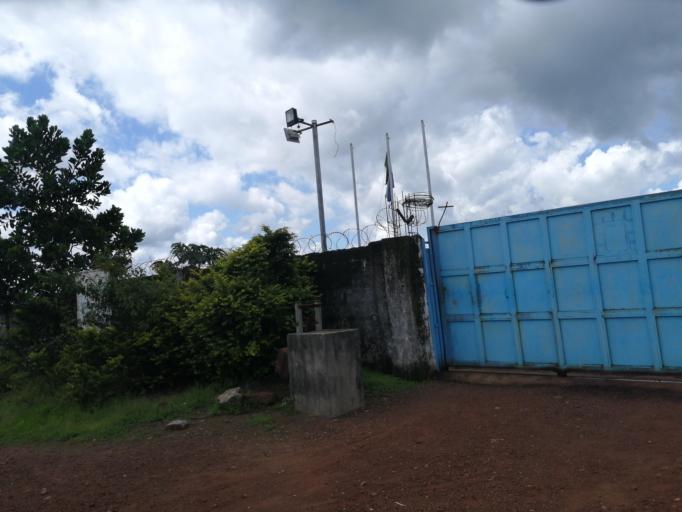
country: SL
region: Northern Province
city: Port Loko
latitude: 8.7676
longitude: -12.7787
